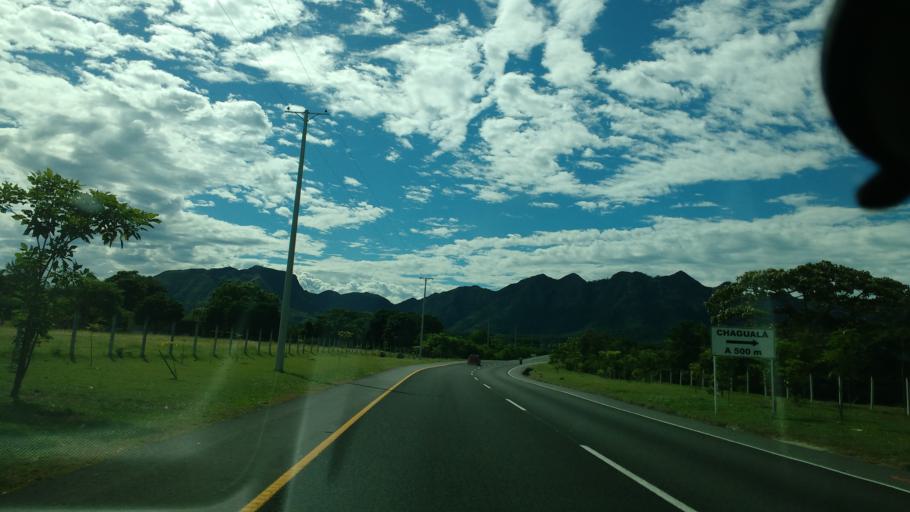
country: CO
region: Tolima
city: Valle de San Juan
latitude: 4.2638
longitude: -74.9973
